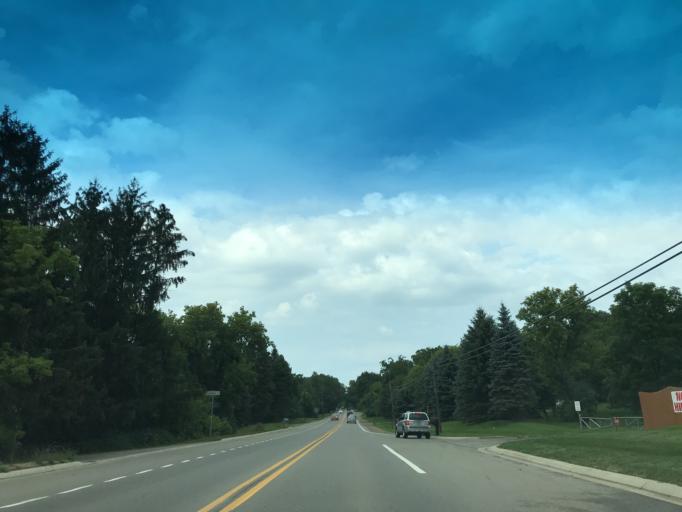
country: US
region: Michigan
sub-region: Oakland County
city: Milford
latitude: 42.5680
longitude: -83.6156
